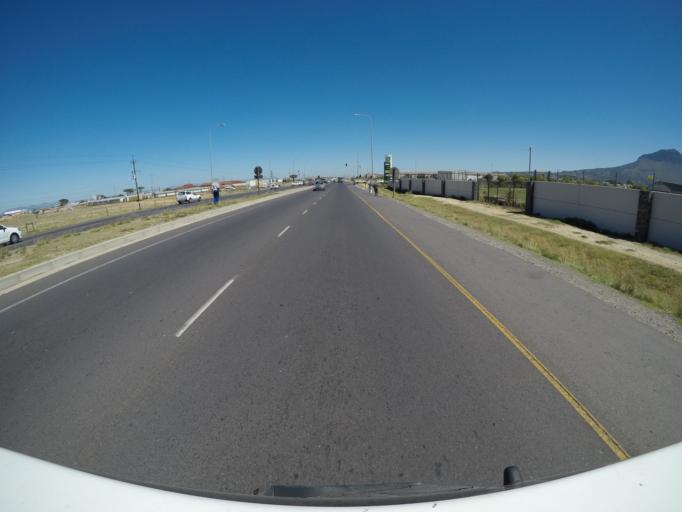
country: ZA
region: Western Cape
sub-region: Overberg District Municipality
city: Grabouw
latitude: -34.1089
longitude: 18.8622
